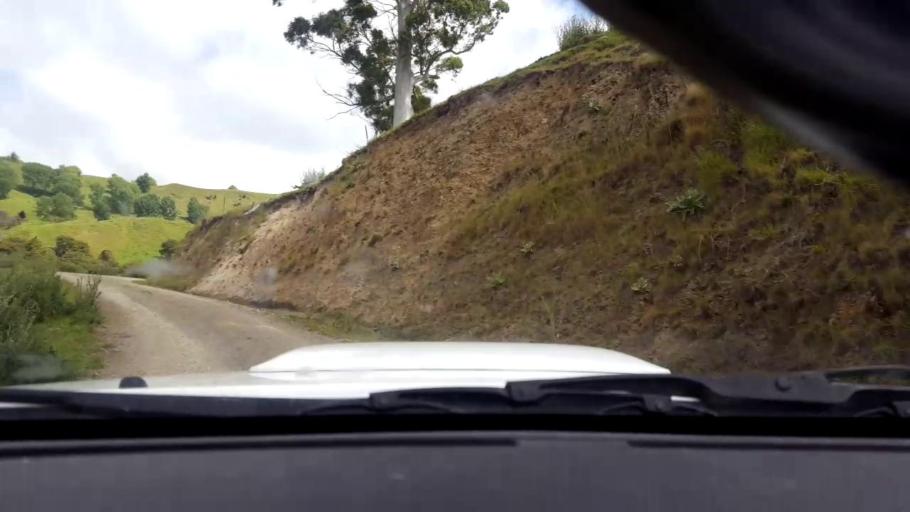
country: NZ
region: Gisborne
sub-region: Gisborne District
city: Gisborne
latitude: -38.4901
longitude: 177.6788
